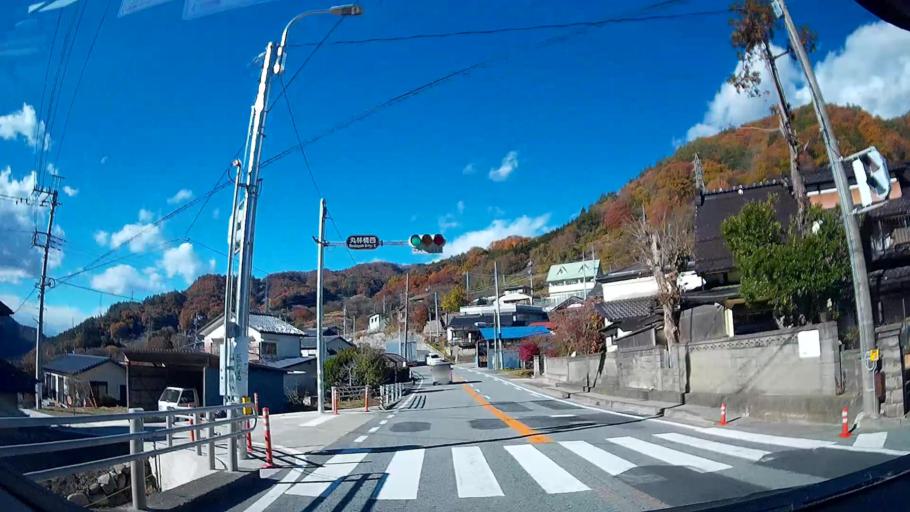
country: JP
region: Yamanashi
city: Enzan
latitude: 35.6394
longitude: 138.7904
